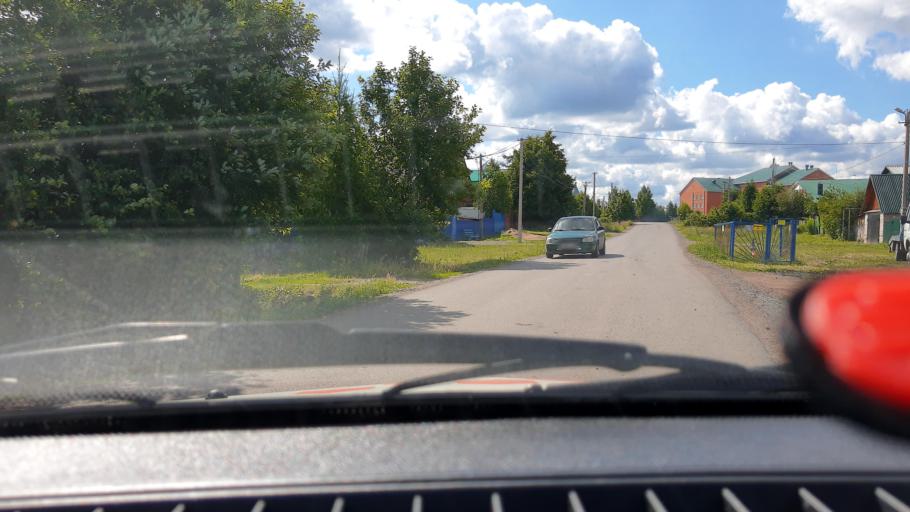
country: RU
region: Bashkortostan
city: Avdon
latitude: 54.4961
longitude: 55.8960
